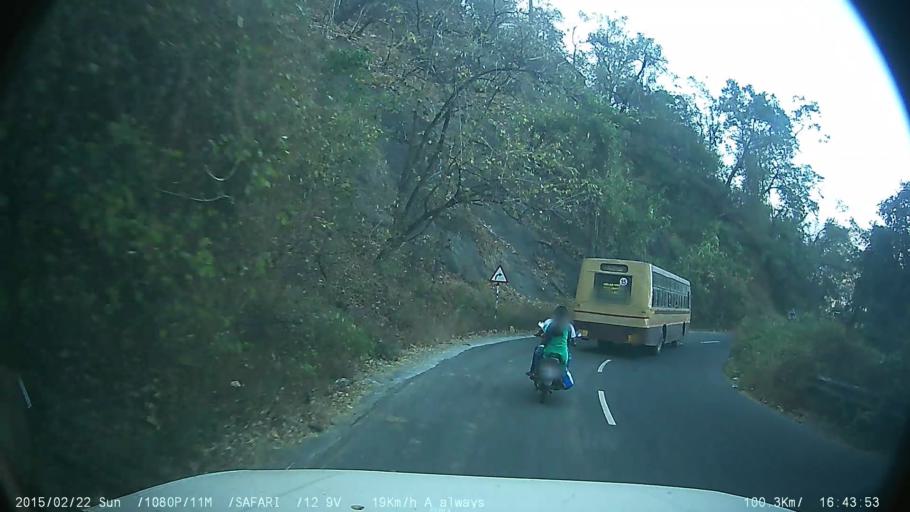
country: IN
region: Tamil Nadu
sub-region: Theni
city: Gudalur
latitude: 9.6206
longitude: 77.1895
